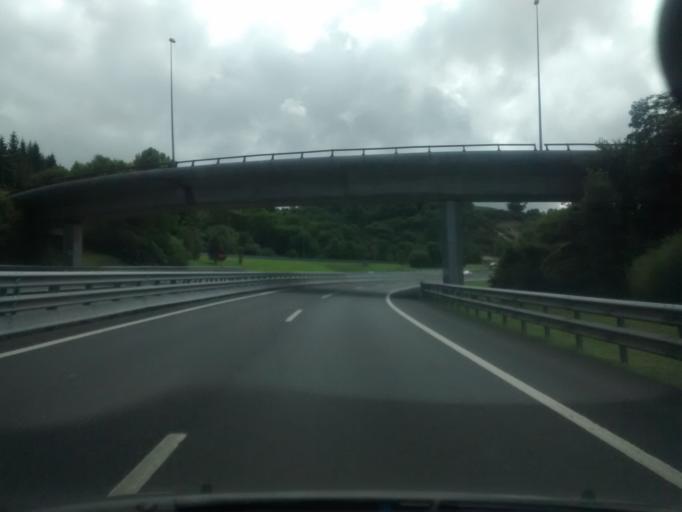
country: ES
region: Basque Country
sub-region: Provincia de Guipuzcoa
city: Lasarte
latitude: 43.2918
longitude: -2.0171
